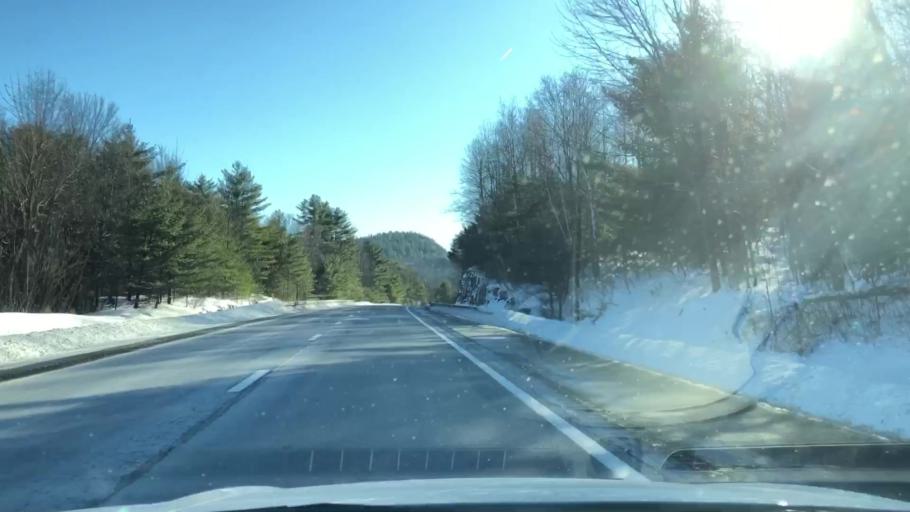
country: US
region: New York
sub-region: Warren County
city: Warrensburg
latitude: 43.7677
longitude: -73.8036
